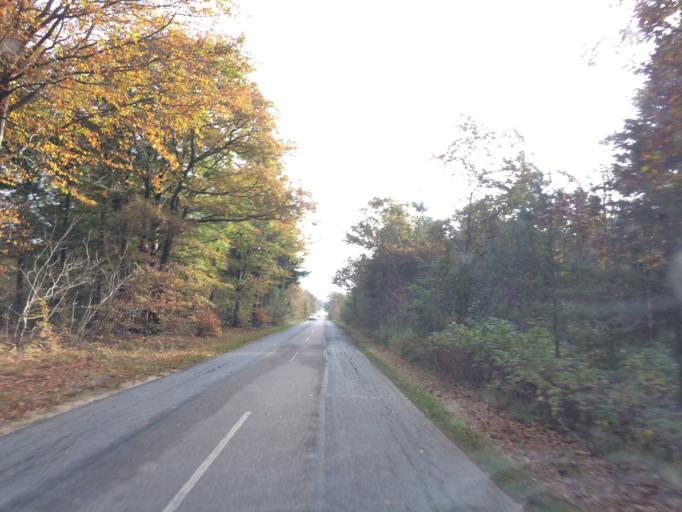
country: DK
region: Central Jutland
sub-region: Holstebro Kommune
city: Holstebro
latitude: 56.3520
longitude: 8.5559
